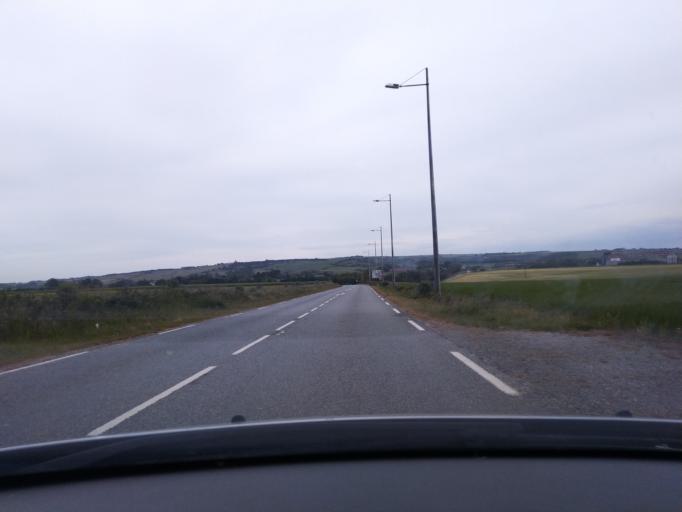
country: FR
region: Nord-Pas-de-Calais
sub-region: Departement du Pas-de-Calais
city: Marquise
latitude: 50.8273
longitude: 1.6973
